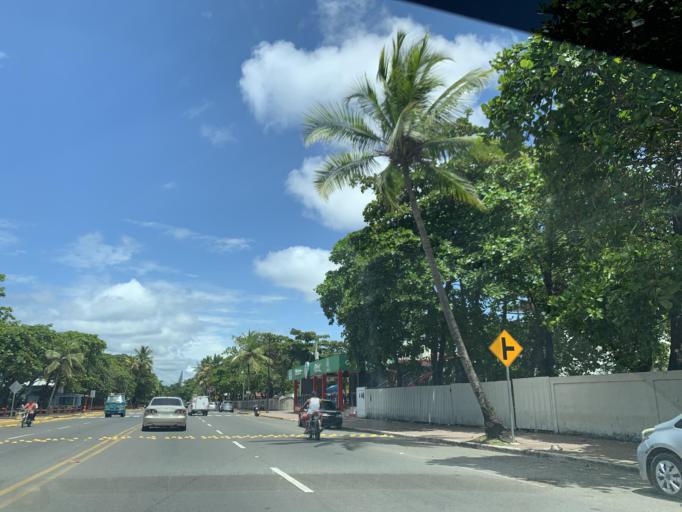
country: DO
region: Puerto Plata
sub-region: Puerto Plata
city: Puerto Plata
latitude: 19.7924
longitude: -70.6759
